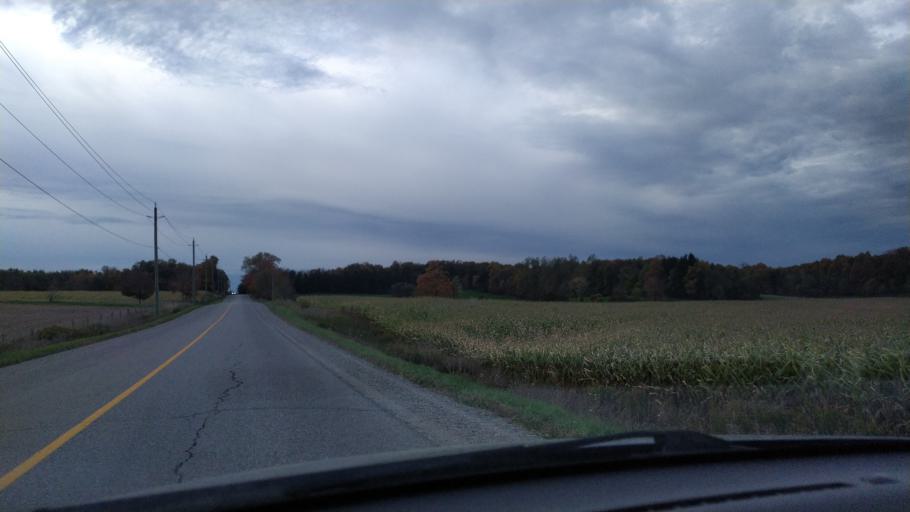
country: CA
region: Ontario
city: Waterloo
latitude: 43.5018
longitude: -80.6276
